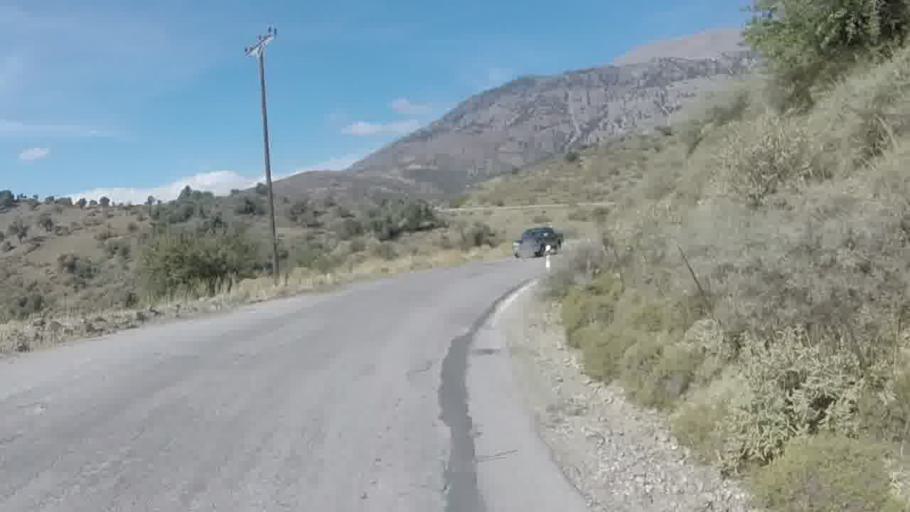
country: GR
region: Crete
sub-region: Nomos Rethymnis
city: Agia Galini
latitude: 35.1769
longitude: 24.7378
